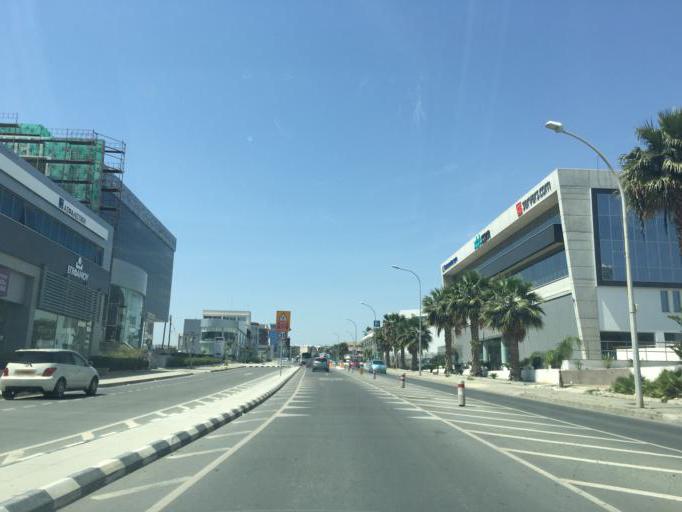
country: CY
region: Limassol
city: Limassol
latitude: 34.6978
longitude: 33.0639
